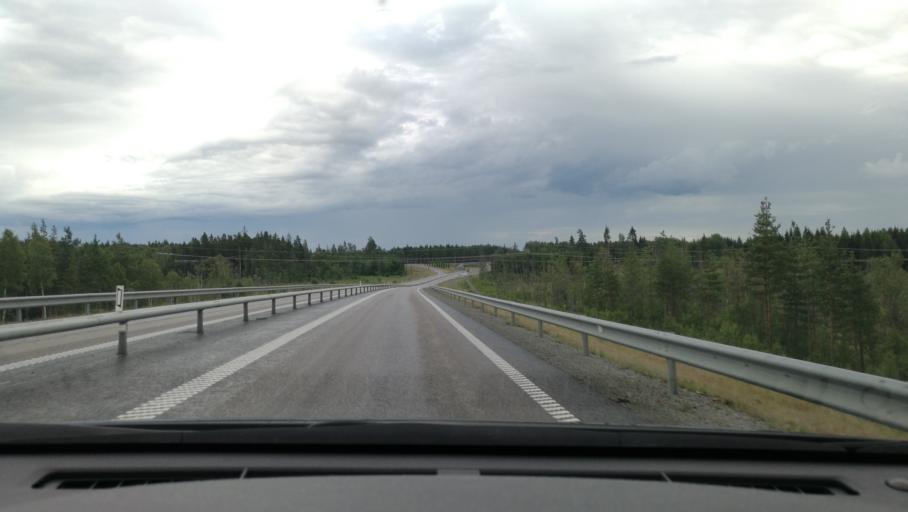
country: SE
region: Soedermanland
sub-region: Katrineholms Kommun
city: Katrineholm
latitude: 58.9988
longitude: 16.2529
